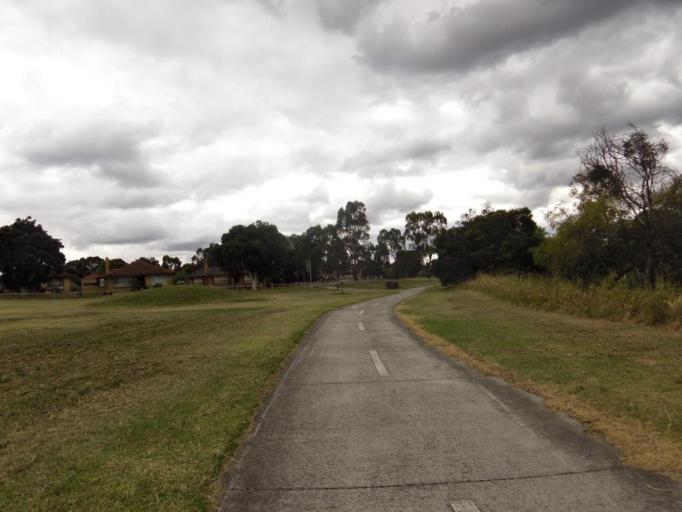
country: AU
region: Victoria
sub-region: Darebin
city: Kingsbury
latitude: -37.7124
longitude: 145.0253
